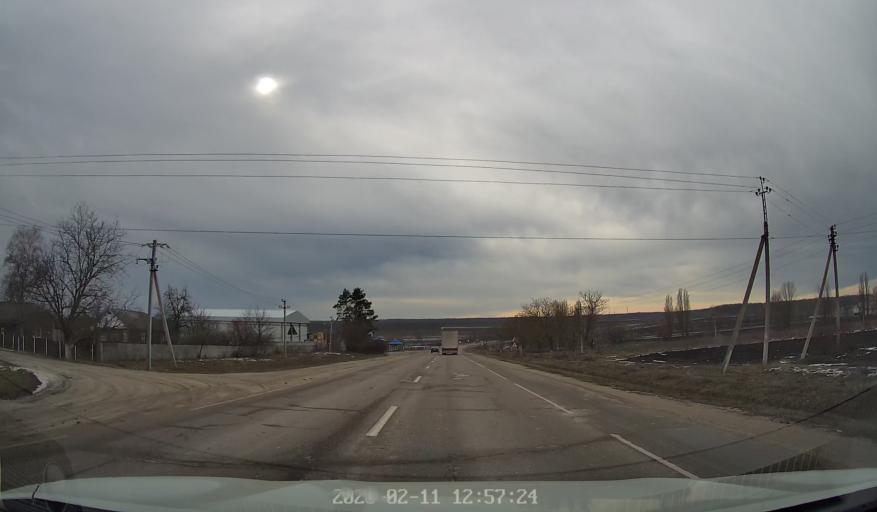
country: MD
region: Briceni
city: Briceni
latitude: 48.3412
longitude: 27.0674
